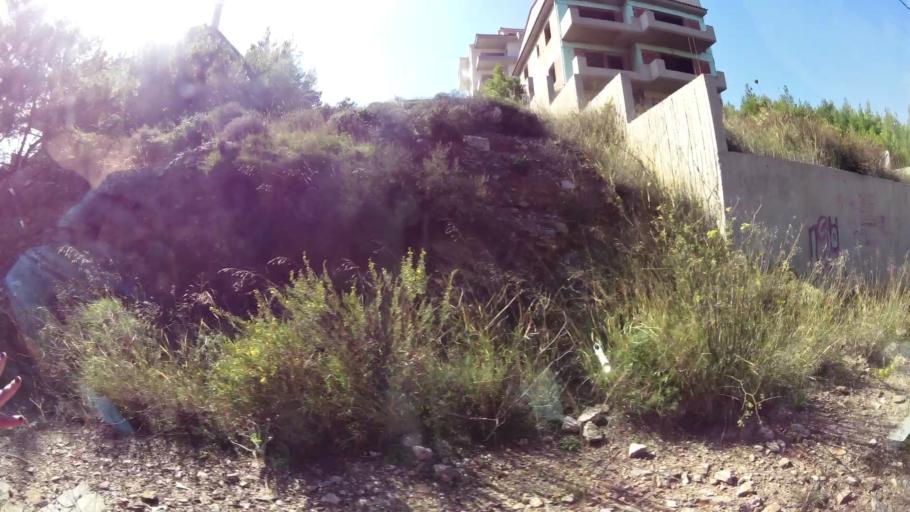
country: GR
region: Attica
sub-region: Nomarchia Anatolikis Attikis
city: Dioni
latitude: 38.0346
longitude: 23.9437
